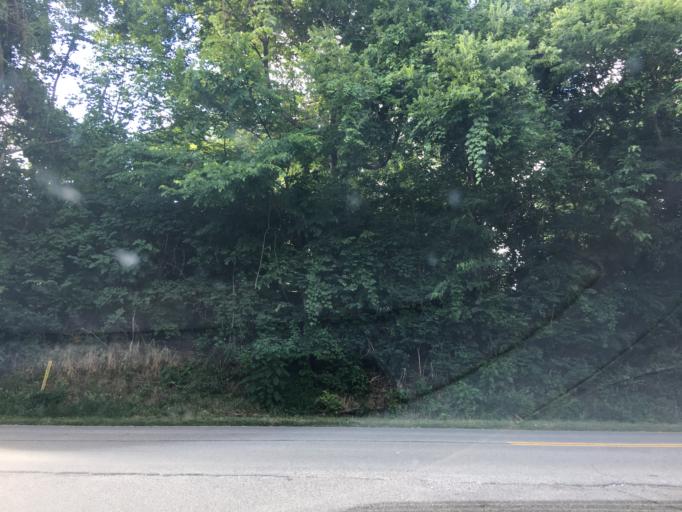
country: US
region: Tennessee
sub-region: Davidson County
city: Oak Hill
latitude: 36.0979
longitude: -86.7232
